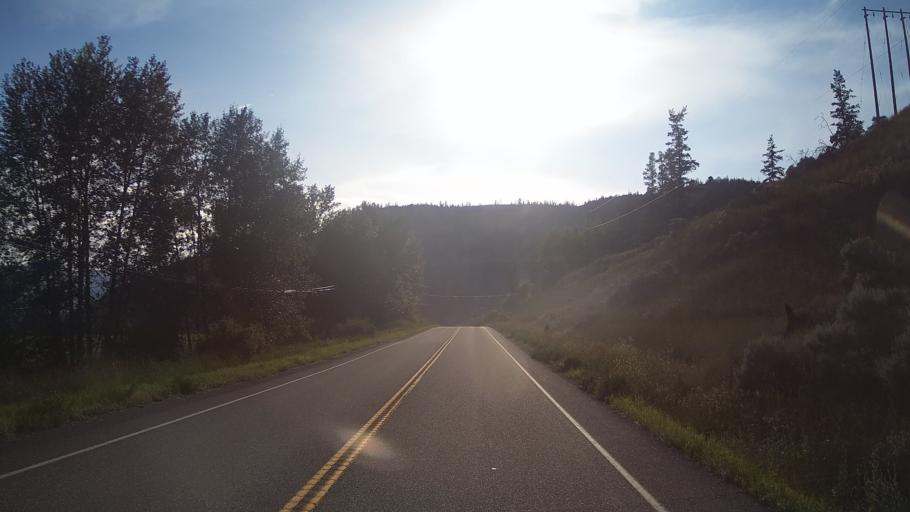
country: CA
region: British Columbia
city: Lillooet
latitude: 50.8986
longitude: -121.7802
